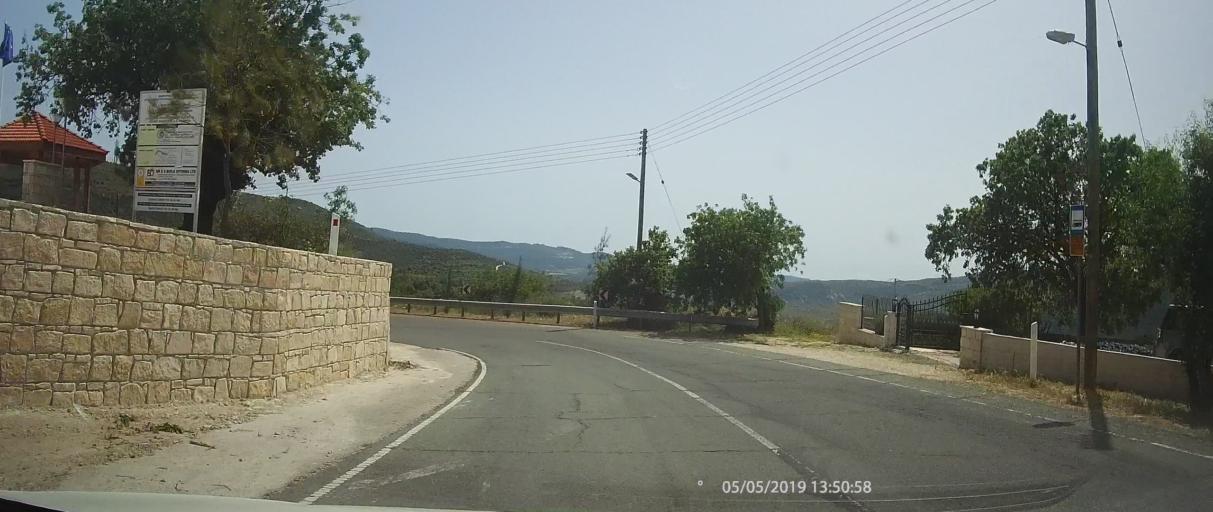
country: CY
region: Limassol
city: Pachna
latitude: 34.8387
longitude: 32.7354
